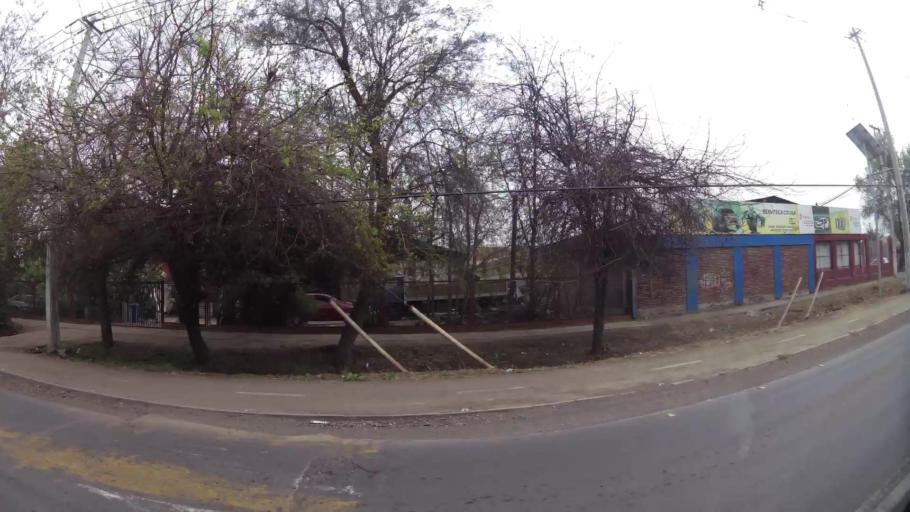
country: CL
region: Santiago Metropolitan
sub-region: Provincia de Chacabuco
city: Chicureo Abajo
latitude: -33.1984
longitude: -70.6786
